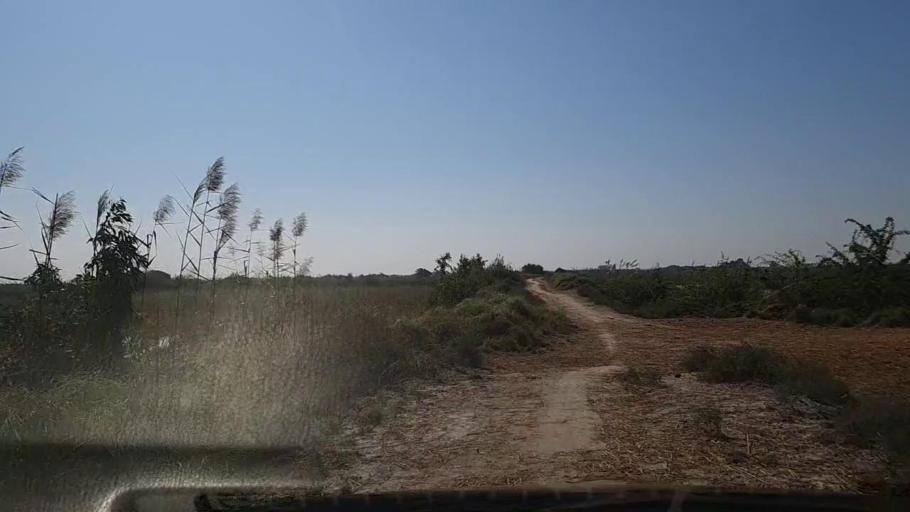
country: PK
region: Sindh
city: Thatta
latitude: 24.6696
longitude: 67.8894
